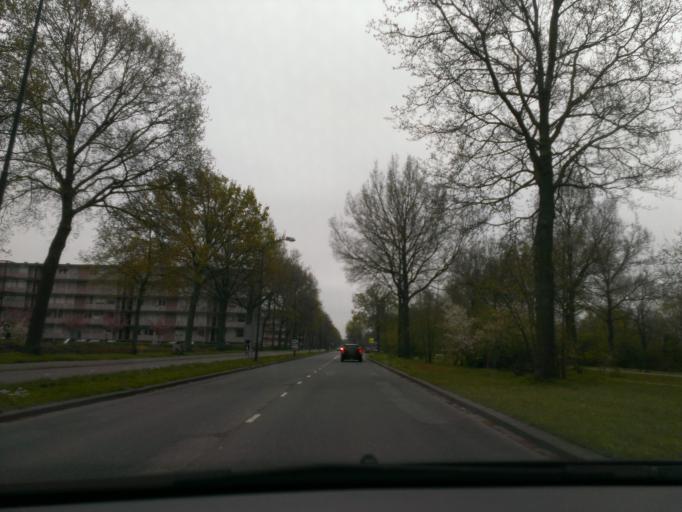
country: NL
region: Gelderland
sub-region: Gemeente Apeldoorn
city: Apeldoorn
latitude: 52.2268
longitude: 5.9877
